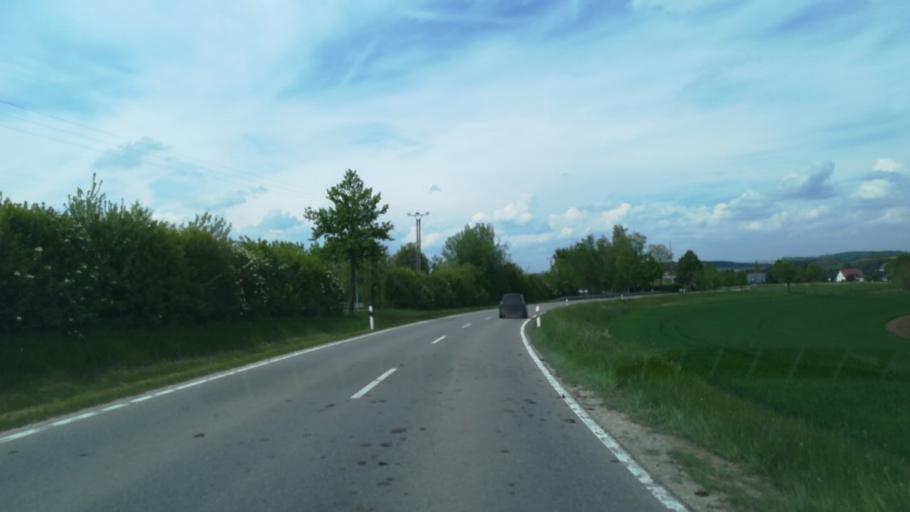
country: DE
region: Baden-Wuerttemberg
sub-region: Freiburg Region
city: Muhlingen
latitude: 47.8894
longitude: 9.0351
